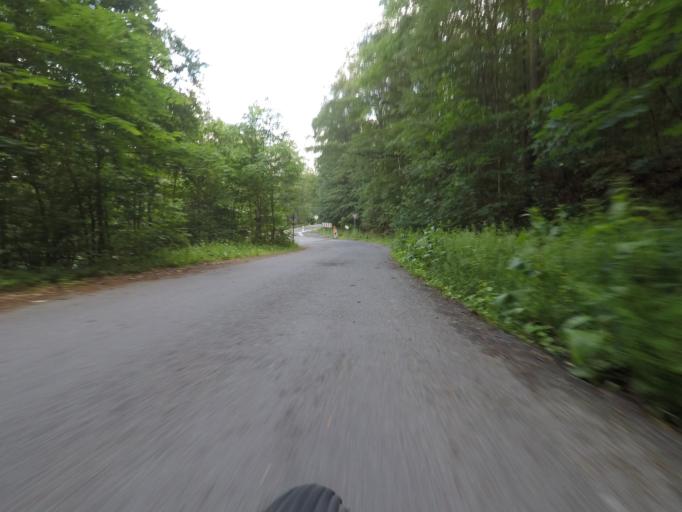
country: DE
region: Hesse
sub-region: Regierungsbezirk Kassel
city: Grossalmerode
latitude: 51.2365
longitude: 9.8549
